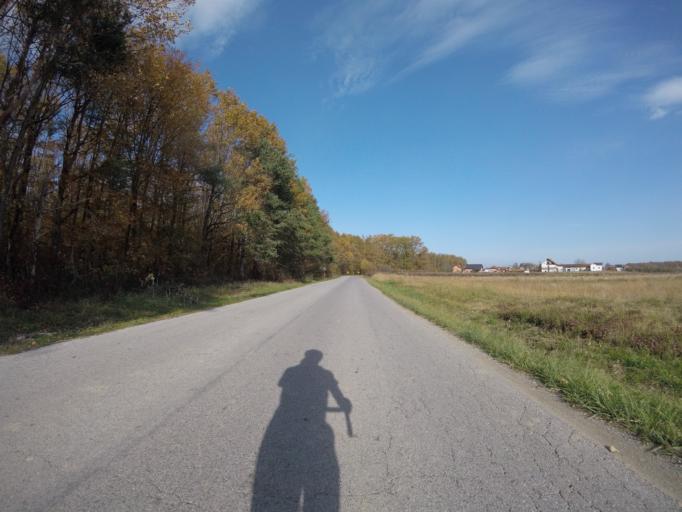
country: HR
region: Zagrebacka
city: Mraclin
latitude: 45.6414
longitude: 16.0471
